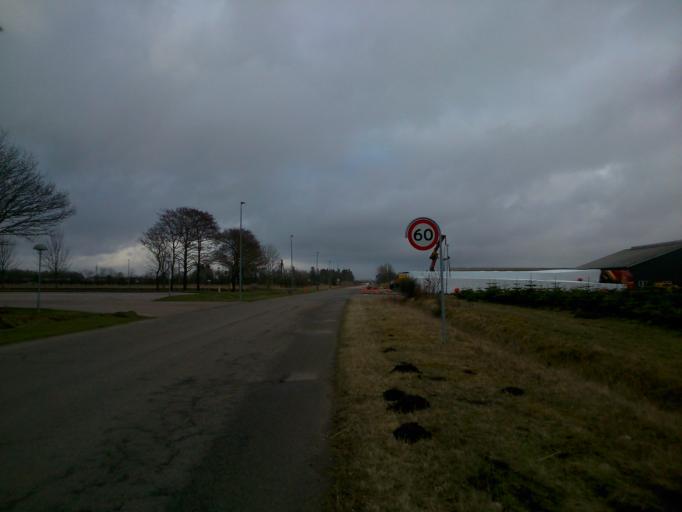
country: DK
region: Central Jutland
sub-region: Ringkobing-Skjern Kommune
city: Skjern
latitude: 55.9649
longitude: 8.4961
